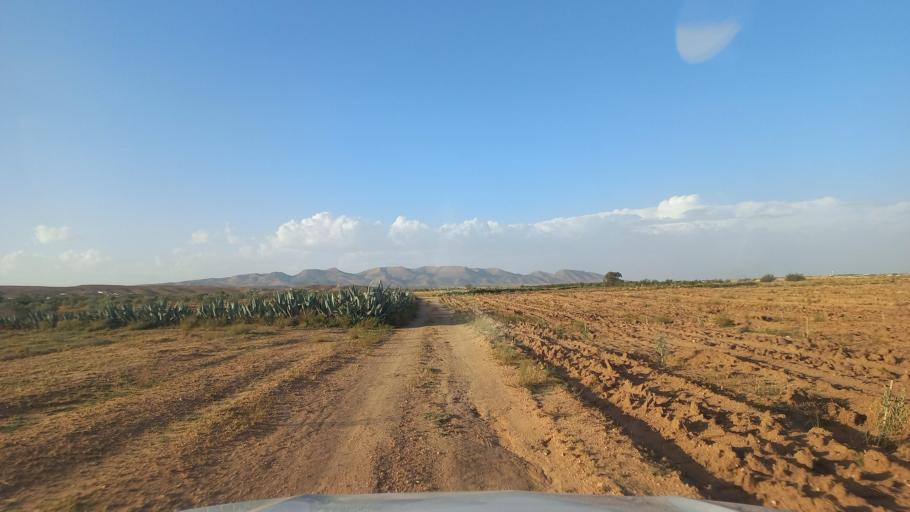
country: TN
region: Al Qasrayn
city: Sbiba
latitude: 35.3634
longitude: 9.0211
